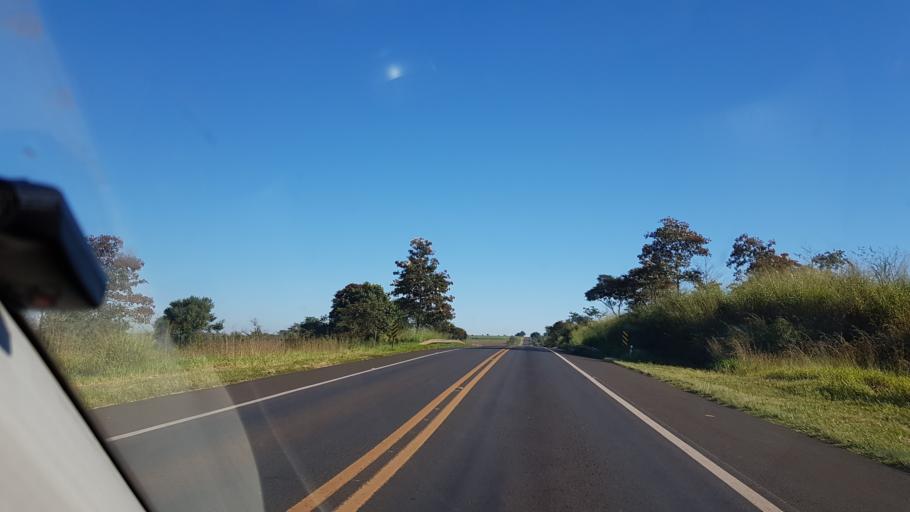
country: BR
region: Sao Paulo
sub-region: Assis
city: Assis
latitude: -22.6073
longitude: -50.4713
